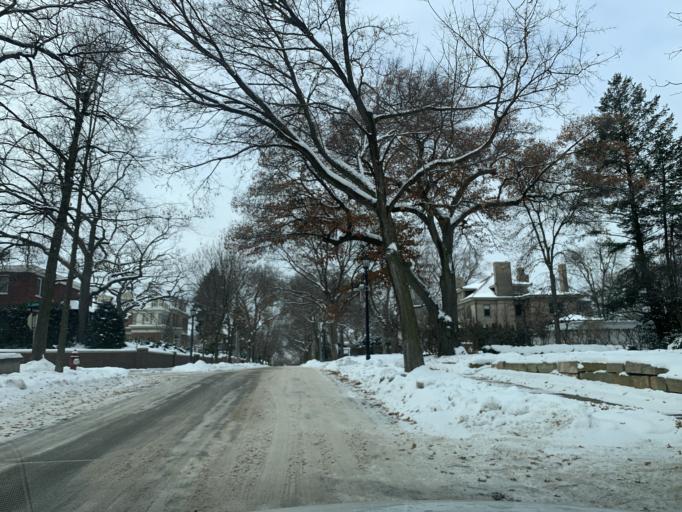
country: US
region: Minnesota
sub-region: Hennepin County
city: Minneapolis
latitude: 44.9680
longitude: -93.3003
